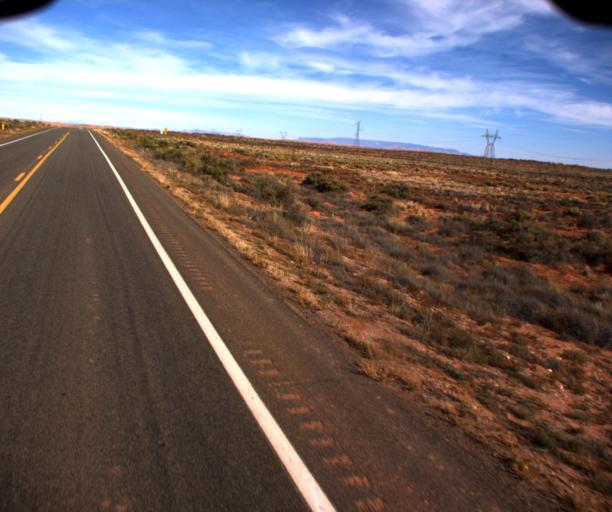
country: US
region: Arizona
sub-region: Navajo County
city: Kayenta
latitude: 36.8023
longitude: -109.9207
